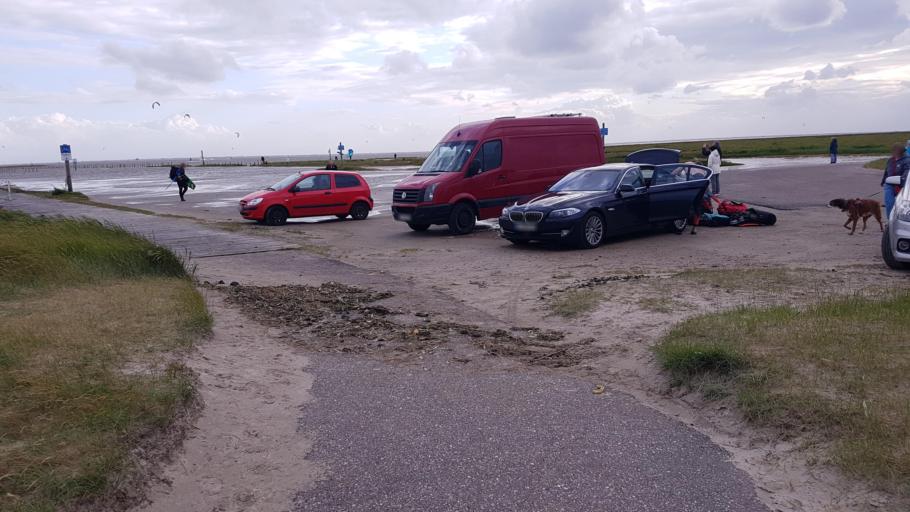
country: DE
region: Schleswig-Holstein
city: Sankt Peter-Ording
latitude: 54.2792
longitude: 8.6570
